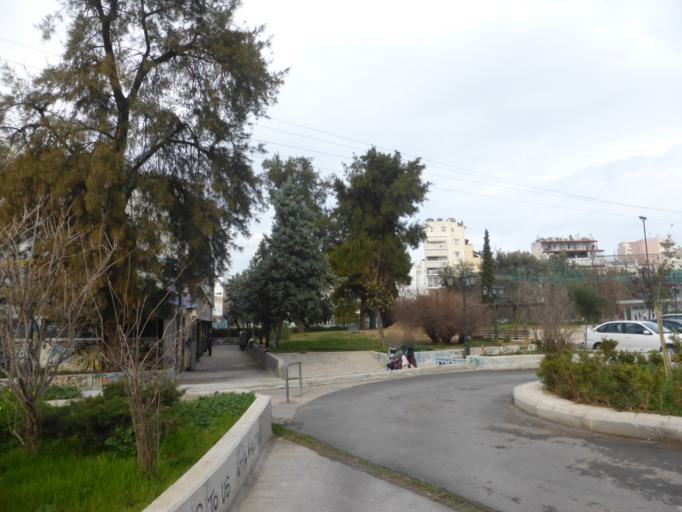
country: GR
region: Attica
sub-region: Nomarchia Athinas
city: Kallithea
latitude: 37.9611
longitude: 23.7020
